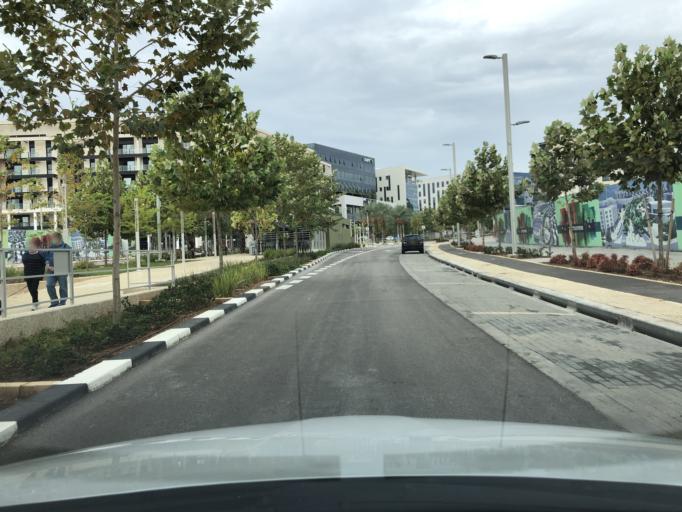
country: IL
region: Central District
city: Modiin
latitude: 31.9027
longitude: 35.0086
